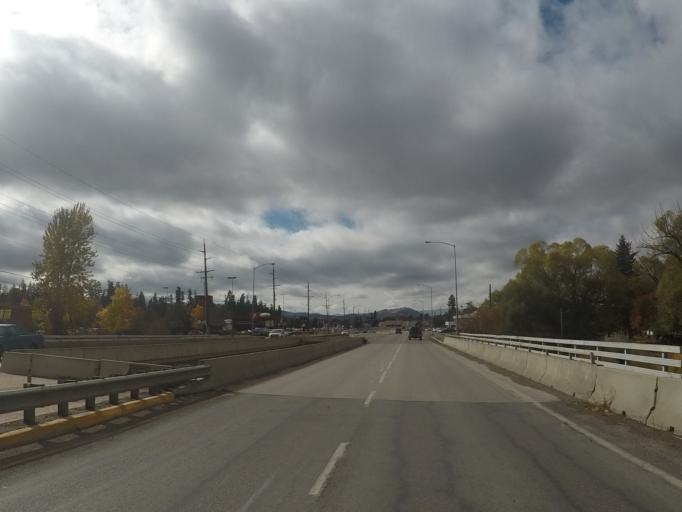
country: US
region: Montana
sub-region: Flathead County
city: Evergreen
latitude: 48.2119
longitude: -114.2846
